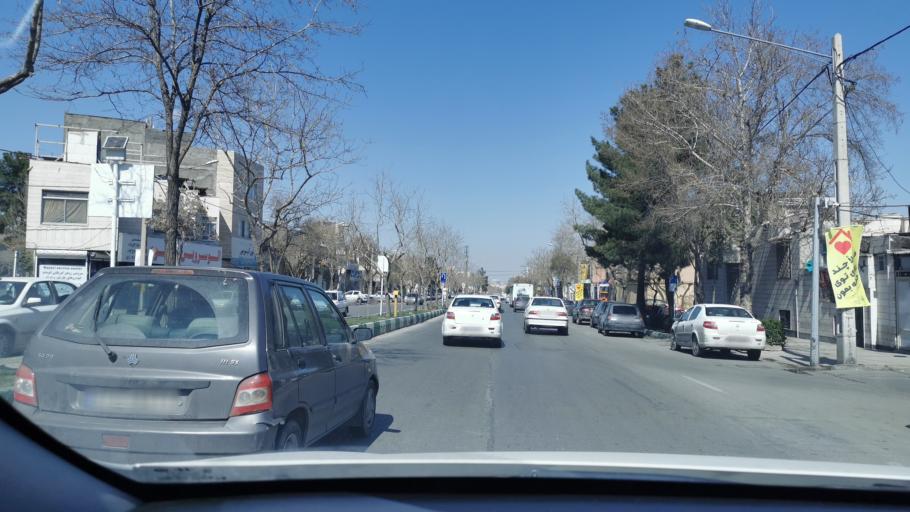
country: IR
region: Razavi Khorasan
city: Mashhad
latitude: 36.2712
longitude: 59.5756
